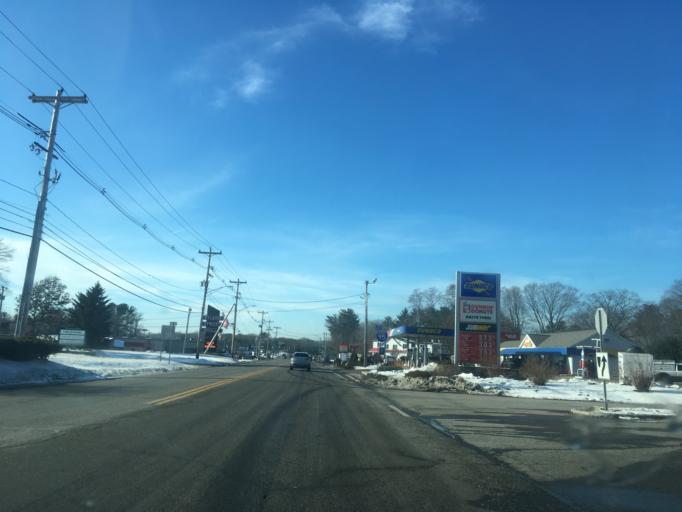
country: US
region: Massachusetts
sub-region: Essex County
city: Salisbury
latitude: 42.8442
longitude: -70.8940
